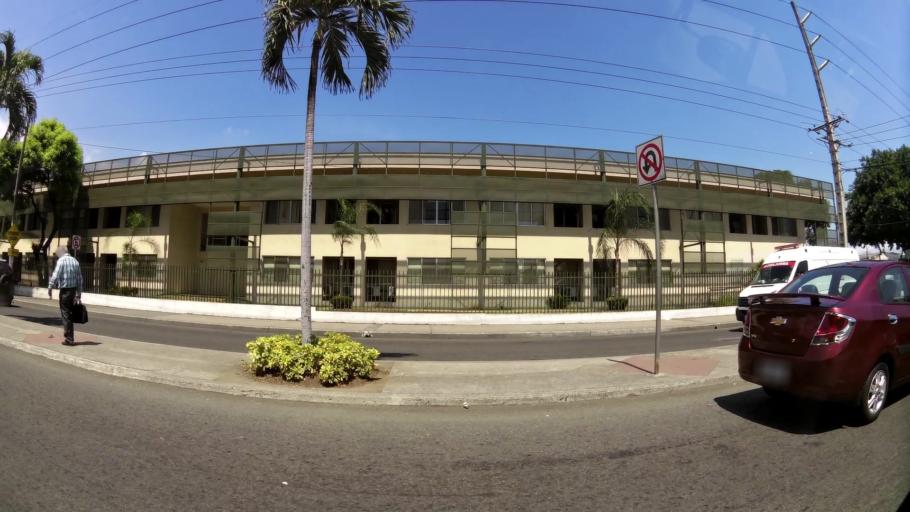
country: EC
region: Guayas
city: Guayaquil
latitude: -2.2302
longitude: -79.8990
